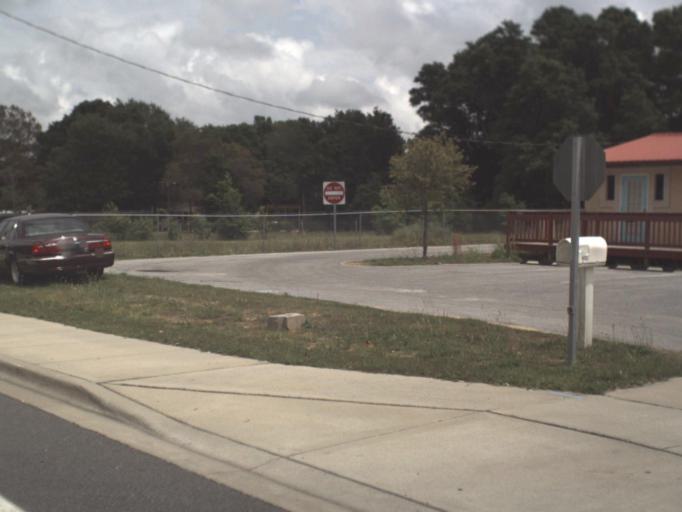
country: US
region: Florida
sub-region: Santa Rosa County
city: Bagdad
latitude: 30.5937
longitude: -87.0805
